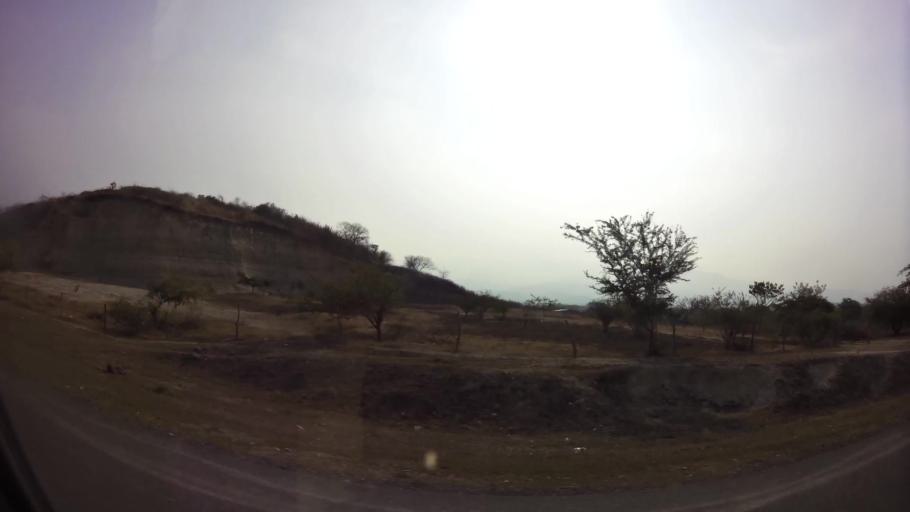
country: HN
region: Comayagua
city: Comayagua
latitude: 14.4503
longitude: -87.6631
